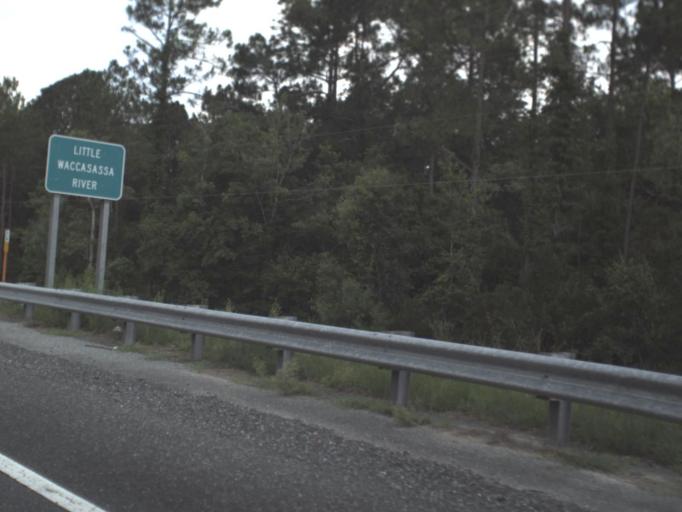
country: US
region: Florida
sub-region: Levy County
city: Bronson
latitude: 29.4769
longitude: -82.6861
